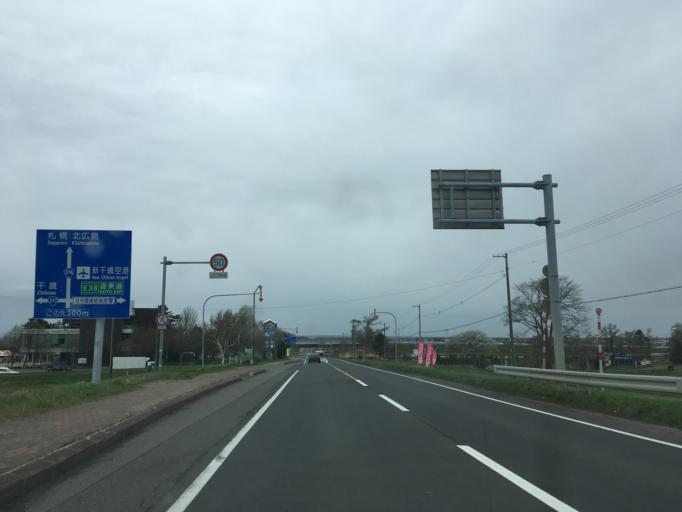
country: JP
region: Hokkaido
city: Chitose
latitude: 42.9496
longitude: 141.7189
